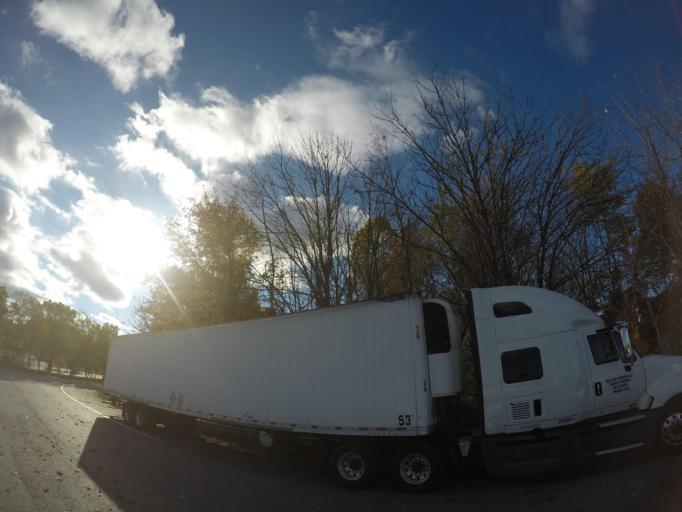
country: US
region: Maryland
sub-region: Carroll County
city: Mount Airy
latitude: 39.3547
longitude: -77.1706
